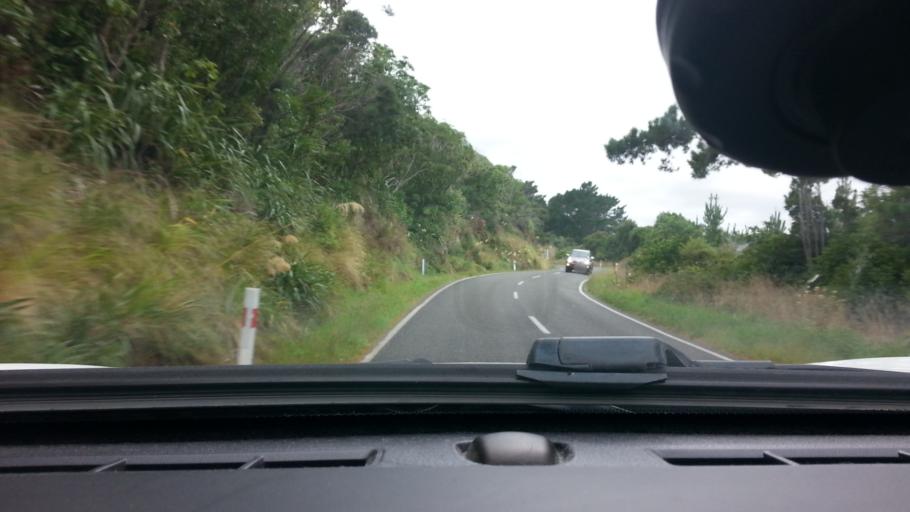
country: NZ
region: Wellington
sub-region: South Wairarapa District
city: Waipawa
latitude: -41.4380
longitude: 175.2195
